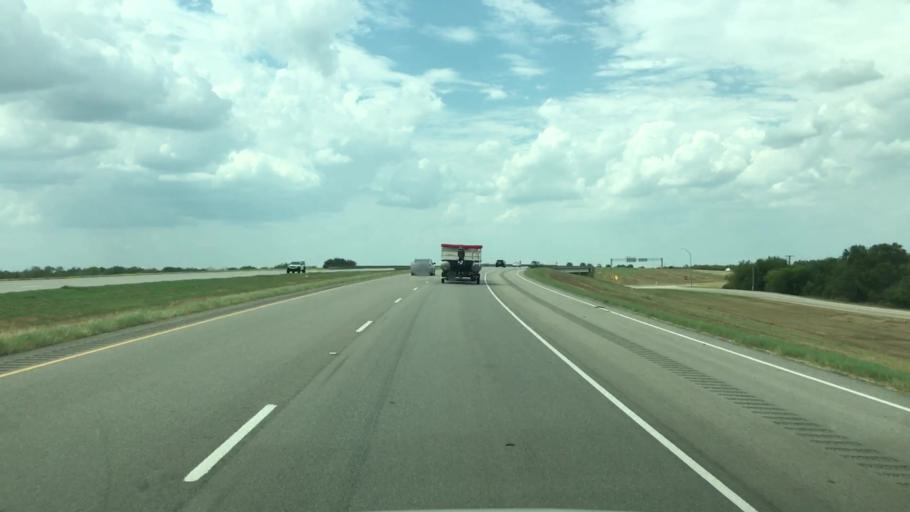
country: US
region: Texas
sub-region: Live Oak County
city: Three Rivers
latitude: 28.5238
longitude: -98.1845
